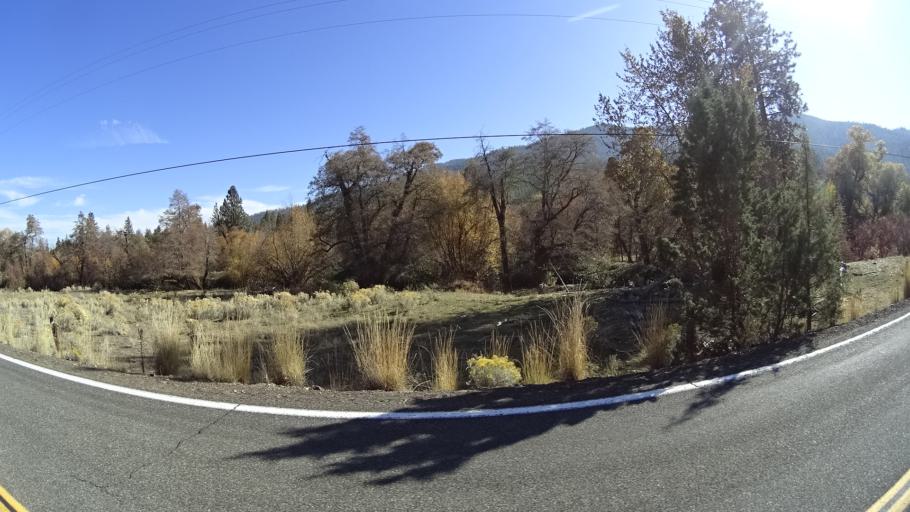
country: US
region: California
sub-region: Siskiyou County
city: Weed
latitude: 41.4799
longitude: -122.5731
